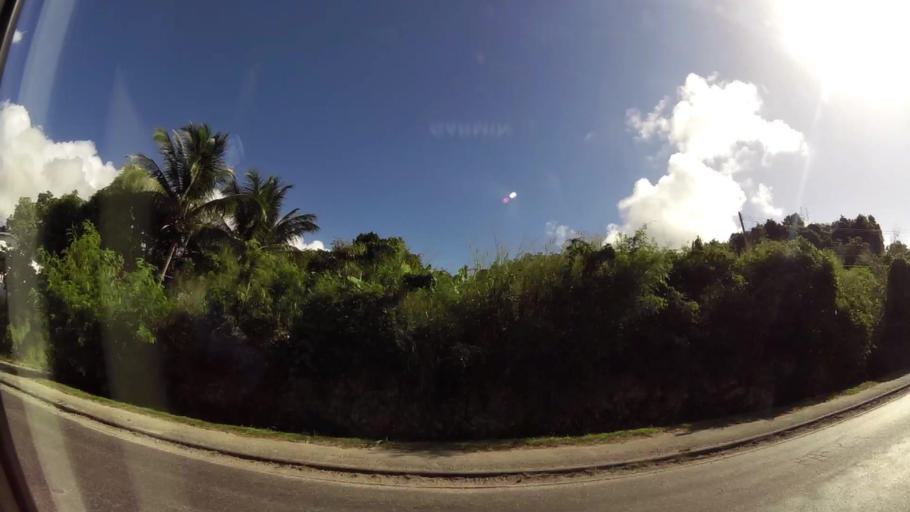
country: BB
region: Saint James
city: Holetown
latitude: 13.2129
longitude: -59.6181
